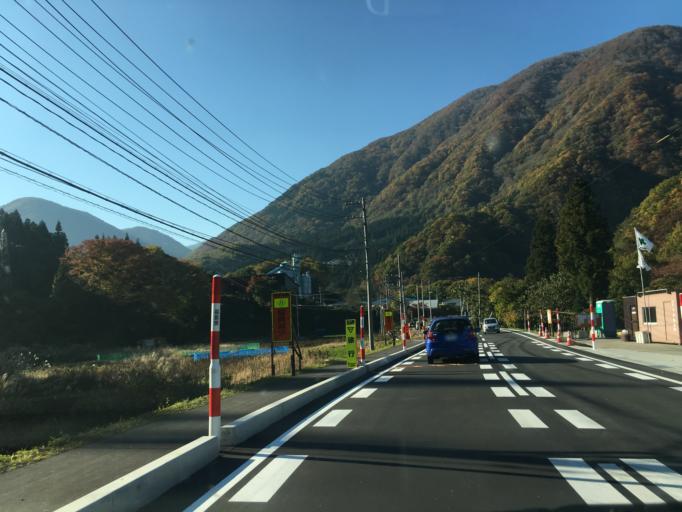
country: JP
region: Fukushima
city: Inawashiro
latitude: 37.3080
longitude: 139.9035
